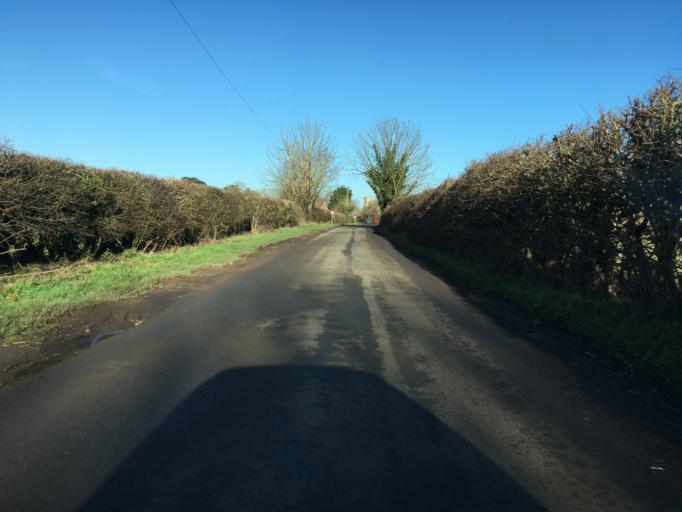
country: GB
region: England
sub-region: Warwickshire
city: Stratford-upon-Avon
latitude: 52.2006
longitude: -1.6629
